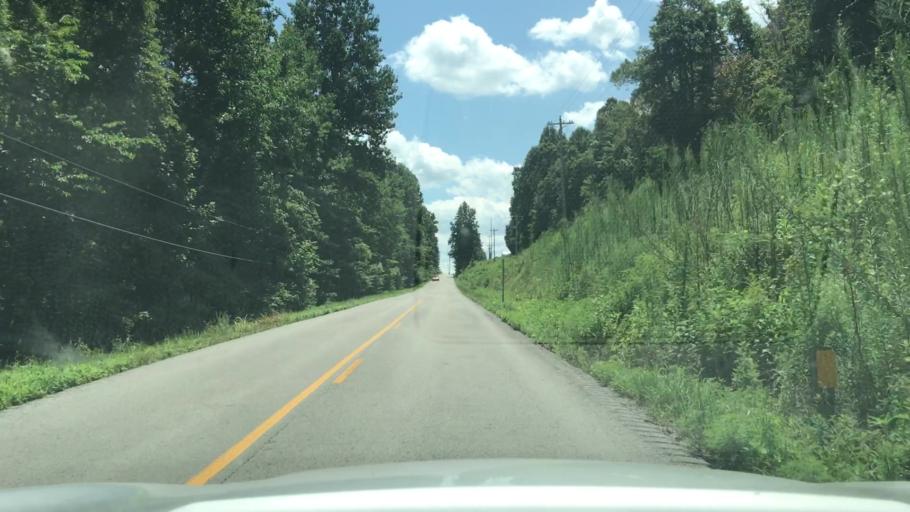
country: US
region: Kentucky
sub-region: Hopkins County
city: Nortonville
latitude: 37.0413
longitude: -87.3495
